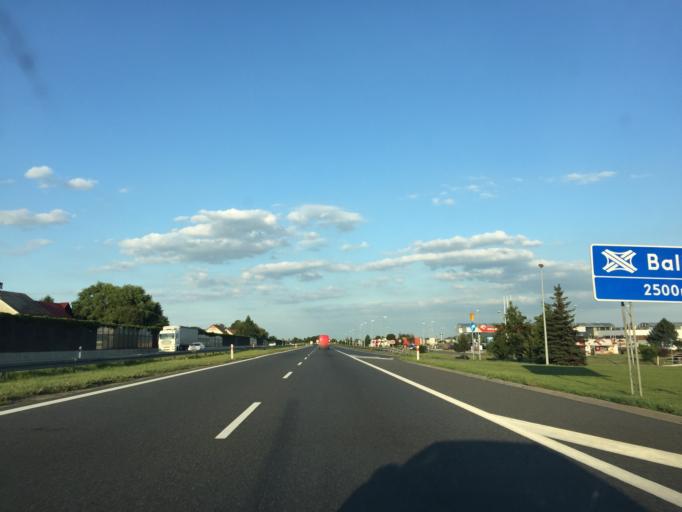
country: PL
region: Lesser Poland Voivodeship
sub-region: Powiat krakowski
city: Mnikow
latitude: 50.0796
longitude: 19.7563
